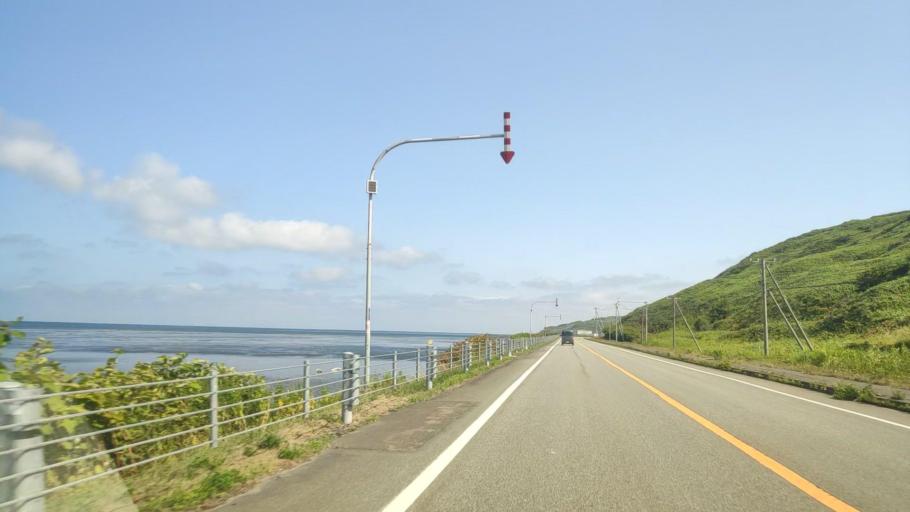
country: JP
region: Hokkaido
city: Makubetsu
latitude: 45.4750
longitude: 141.8741
